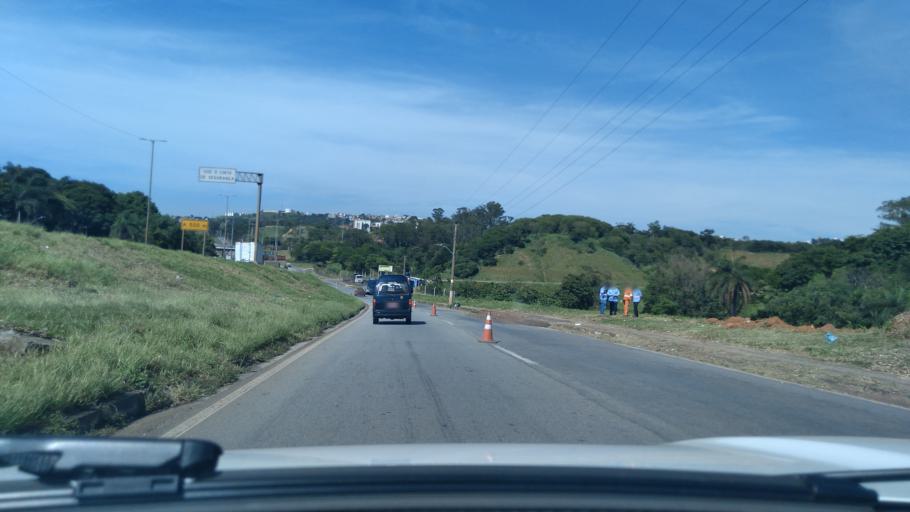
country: BR
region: Minas Gerais
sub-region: Belo Horizonte
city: Belo Horizonte
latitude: -19.8836
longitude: -43.9643
